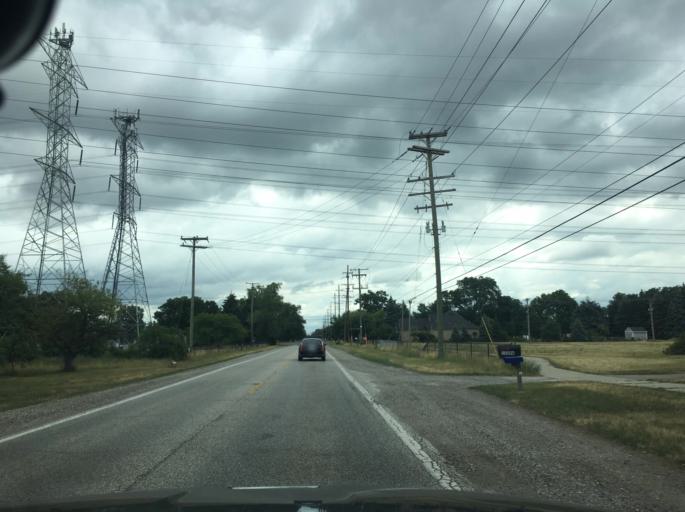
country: US
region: Michigan
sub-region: Macomb County
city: Shelby
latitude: 42.6555
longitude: -83.0043
